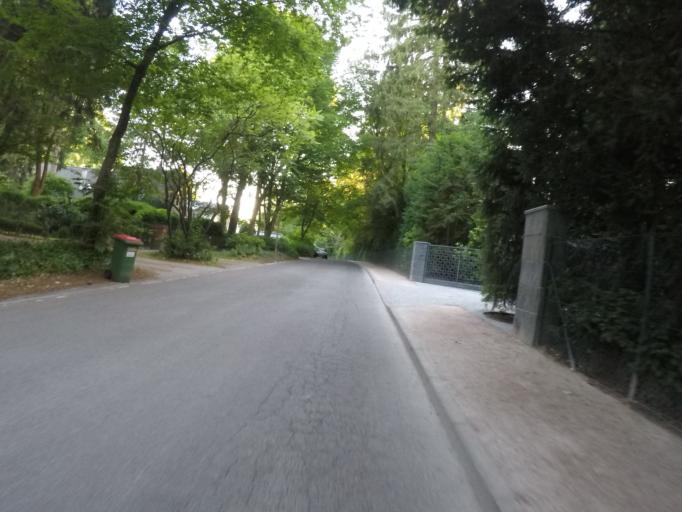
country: DE
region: Hamburg
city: Poppenbuettel
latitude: 53.6658
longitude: 10.0994
